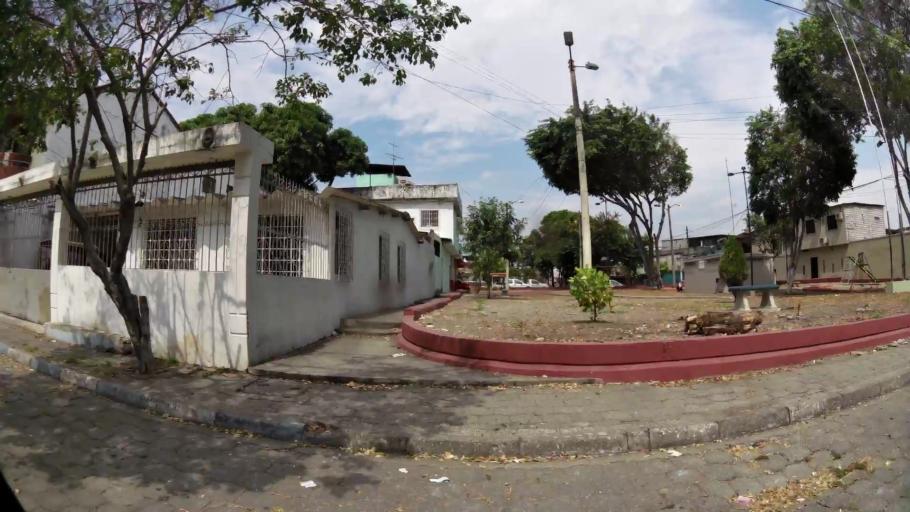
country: EC
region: Guayas
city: Eloy Alfaro
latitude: -2.1254
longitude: -79.9030
